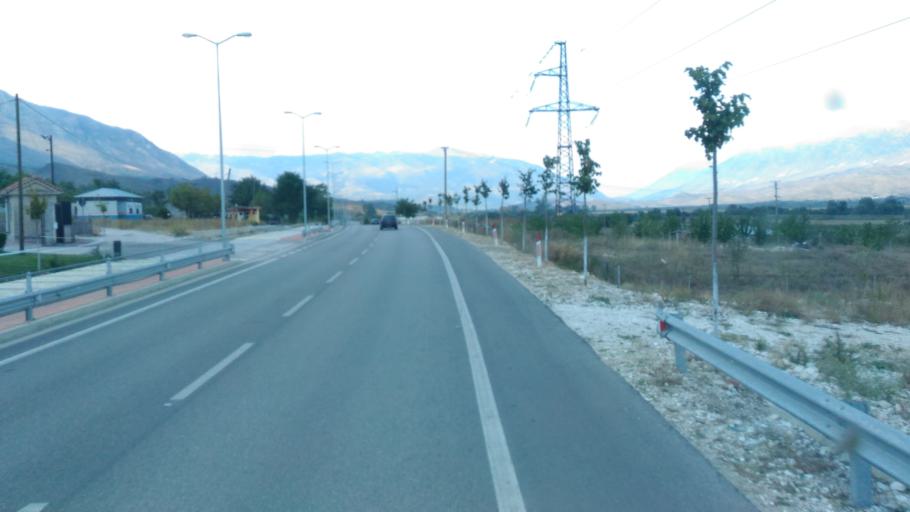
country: AL
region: Gjirokaster
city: Gjirokaster
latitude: 40.0935
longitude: 20.1357
